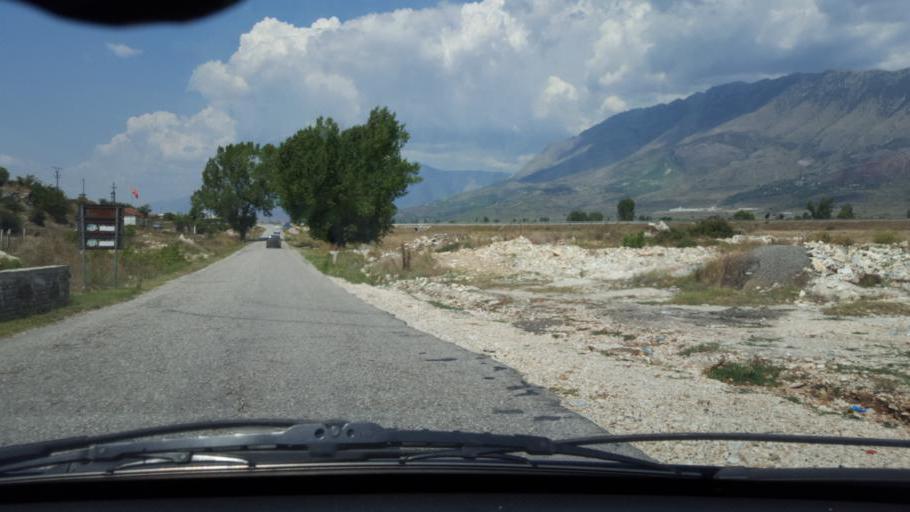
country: AL
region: Gjirokaster
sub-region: Rrethi i Gjirokastres
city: Libohove
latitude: 39.9378
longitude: 20.2677
